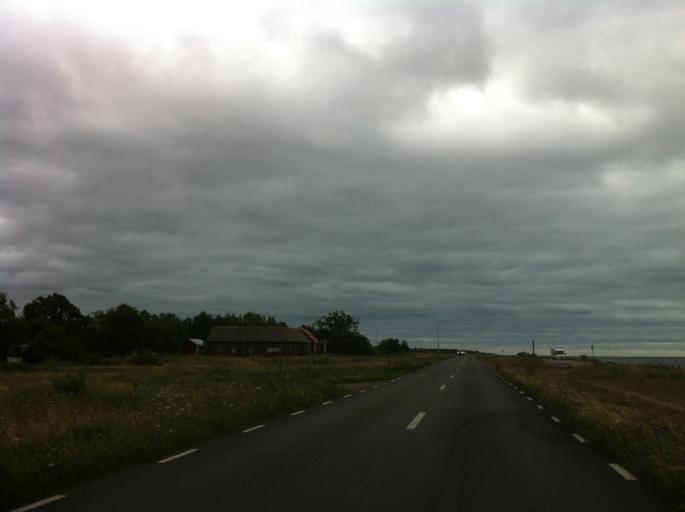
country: SE
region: Kalmar
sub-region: Vasterviks Kommun
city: Vaestervik
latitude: 57.3376
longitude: 17.0142
